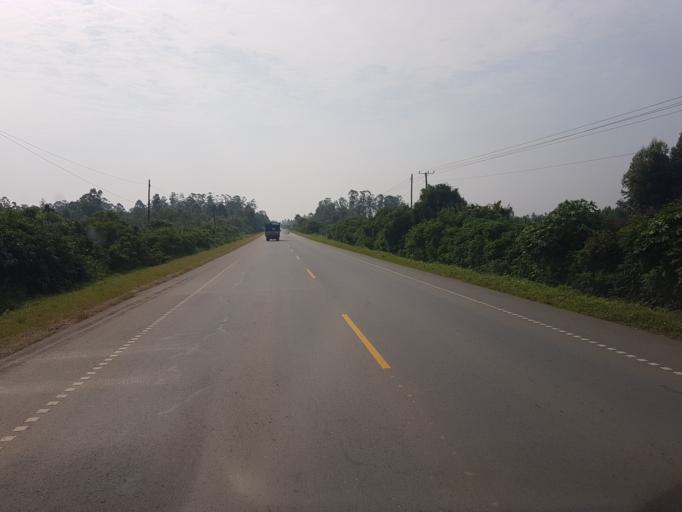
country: UG
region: Western Region
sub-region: Sheema District
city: Kibingo
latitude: -0.6351
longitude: 30.5239
